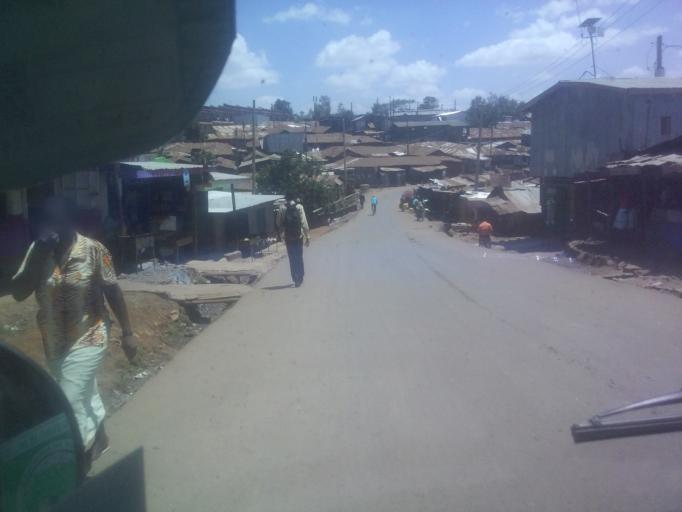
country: KE
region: Nairobi Area
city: Nairobi
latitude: -1.3110
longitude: 36.7893
